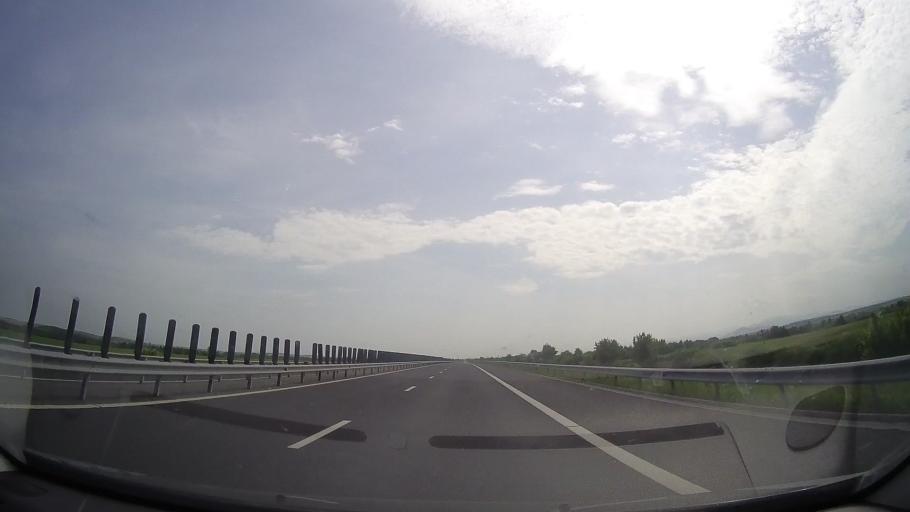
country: RO
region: Timis
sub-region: Comuna Balint
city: Balint
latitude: 45.8047
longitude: 21.9025
